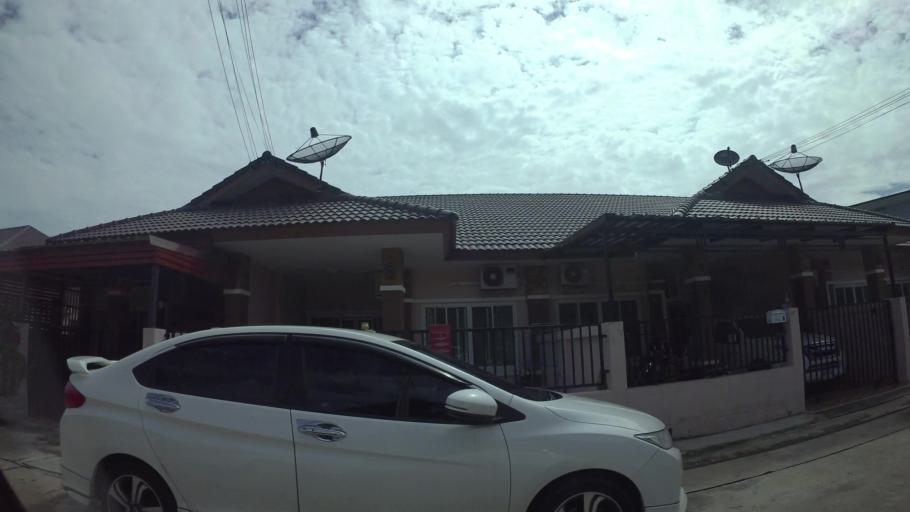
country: TH
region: Rayong
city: Rayong
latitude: 12.6631
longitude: 101.2826
